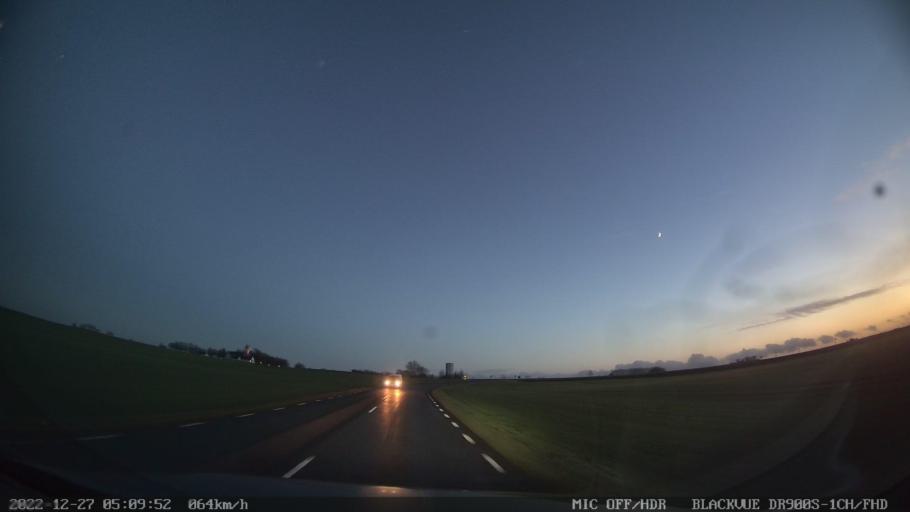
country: SE
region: Skane
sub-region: Simrishamns Kommun
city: Kivik
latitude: 55.5585
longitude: 14.1638
